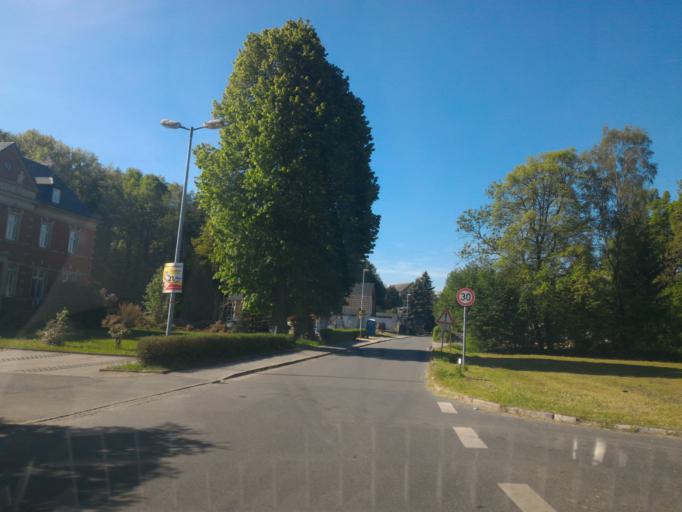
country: DE
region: Saxony
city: Grossschweidnitz
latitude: 51.0661
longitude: 14.6386
